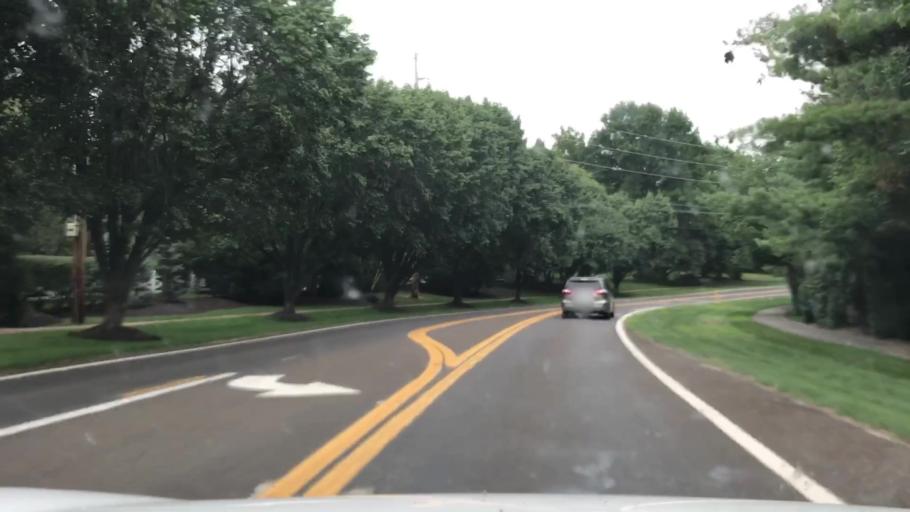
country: US
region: Missouri
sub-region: Saint Louis County
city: Clarkson Valley
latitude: 38.6270
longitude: -90.5928
